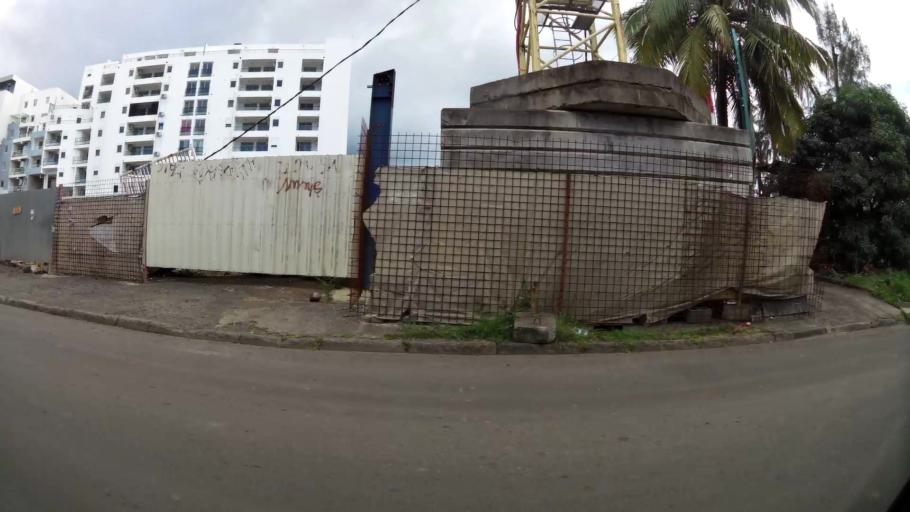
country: RE
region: Reunion
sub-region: Reunion
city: Saint-Denis
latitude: -20.8937
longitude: 55.4739
